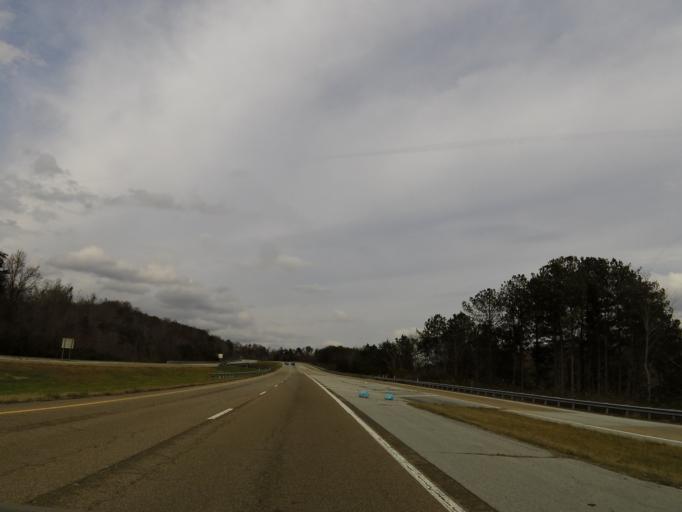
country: US
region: Tennessee
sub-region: Hamilton County
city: Red Bank
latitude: 35.1244
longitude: -85.2953
